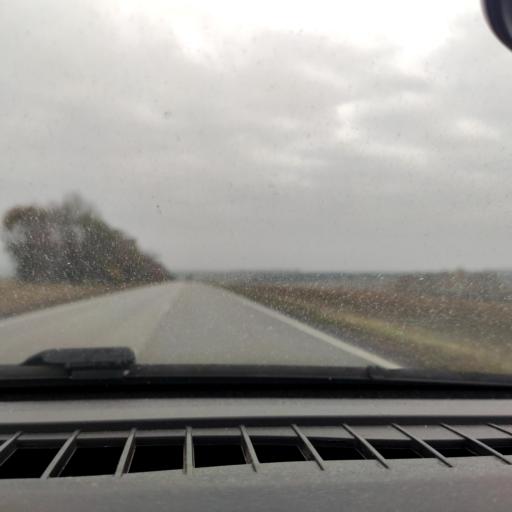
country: RU
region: Belgorod
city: Ilovka
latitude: 50.7627
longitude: 38.7420
